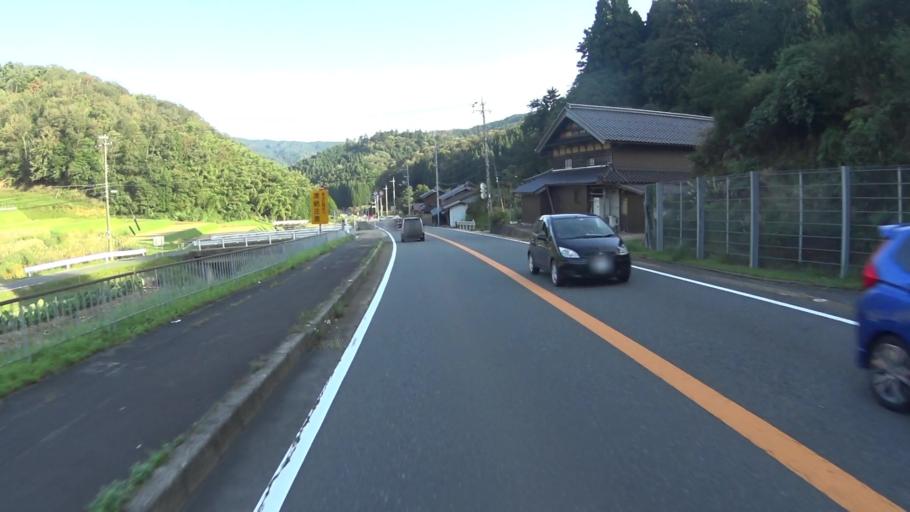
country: JP
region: Kyoto
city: Fukuchiyama
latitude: 35.4270
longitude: 135.0689
